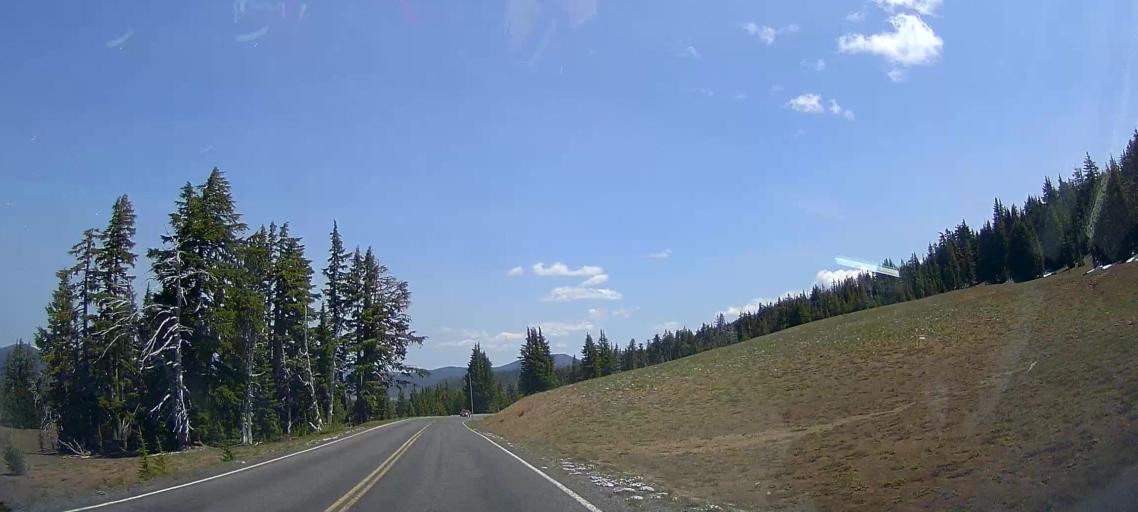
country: US
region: Oregon
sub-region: Jackson County
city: Shady Cove
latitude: 42.9841
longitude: -122.1497
